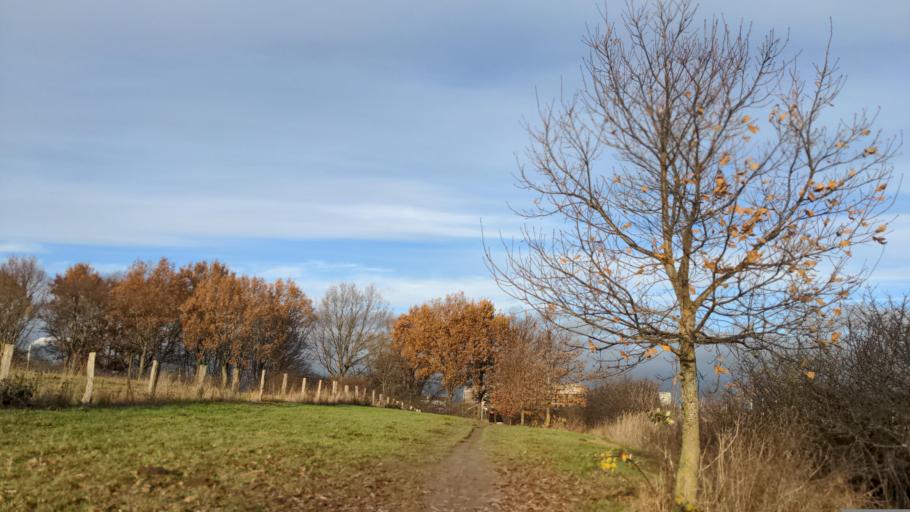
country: DE
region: Schleswig-Holstein
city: Neustadt in Holstein
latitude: 54.0879
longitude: 10.8011
